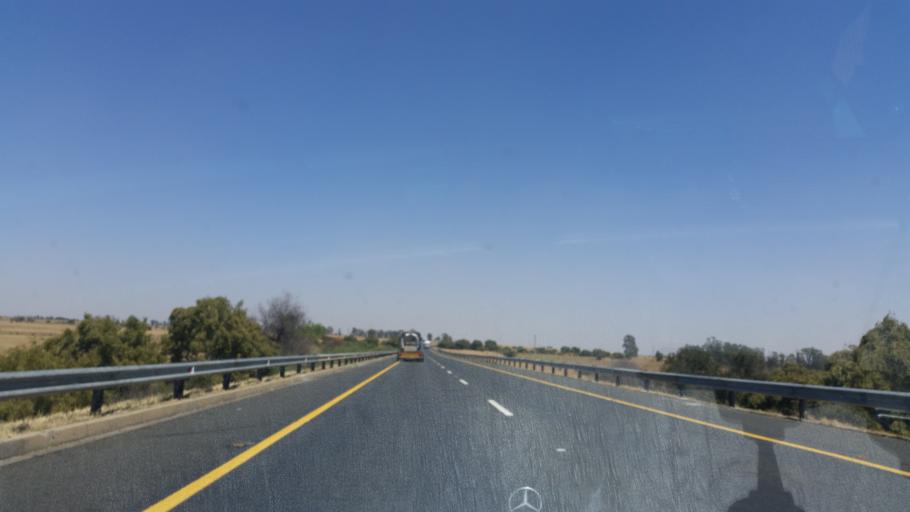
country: ZA
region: Orange Free State
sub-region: Lejweleputswa District Municipality
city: Winburg
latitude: -28.6330
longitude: 26.9016
